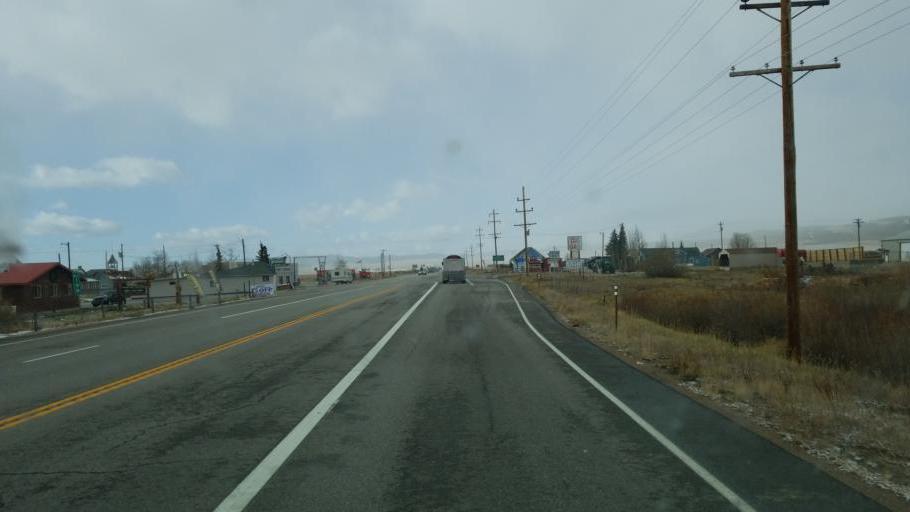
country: US
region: Colorado
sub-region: Park County
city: Fairplay
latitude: 39.3784
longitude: -105.7993
